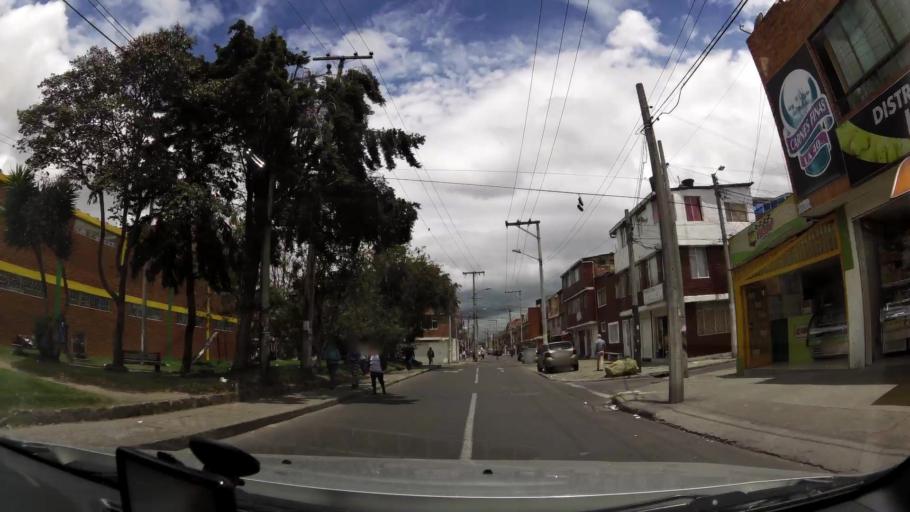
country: CO
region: Bogota D.C.
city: Bogota
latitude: 4.6098
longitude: -74.1125
